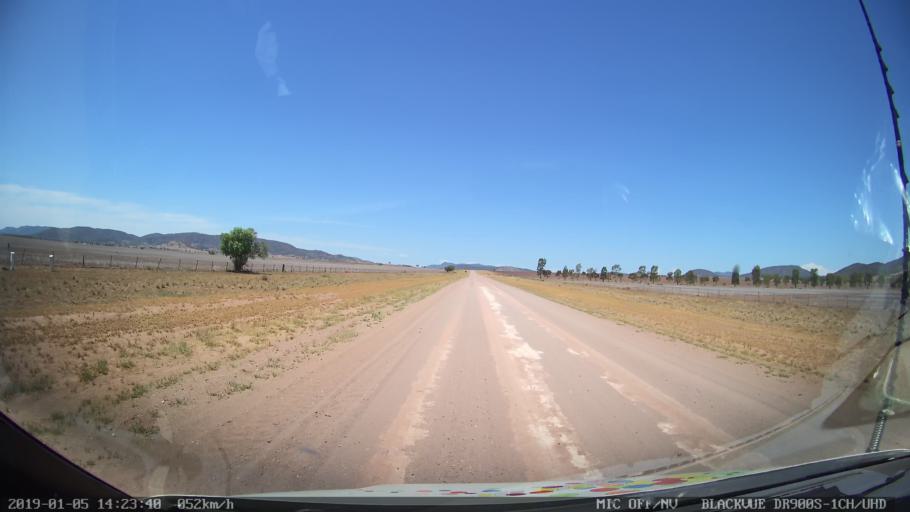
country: AU
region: New South Wales
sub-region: Liverpool Plains
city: Quirindi
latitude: -31.2423
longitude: 150.5323
